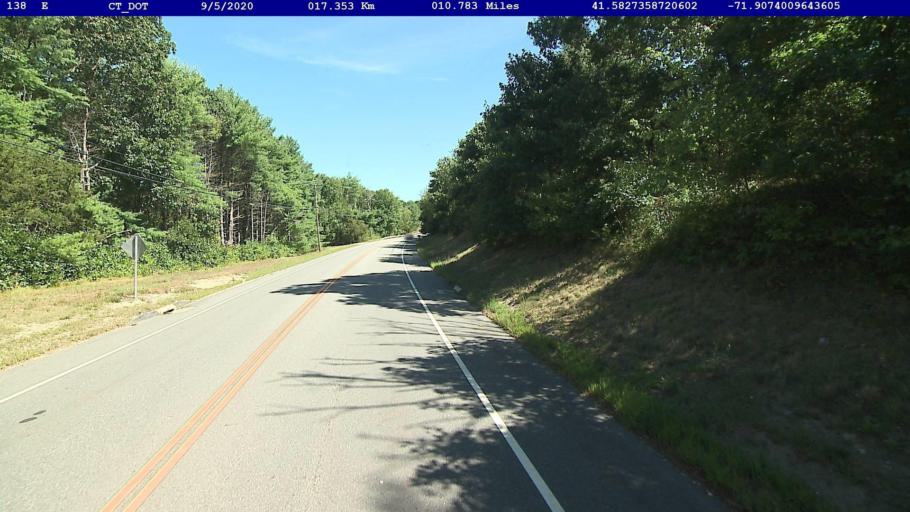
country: US
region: Connecticut
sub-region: New London County
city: Jewett City
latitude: 41.5826
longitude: -71.9074
